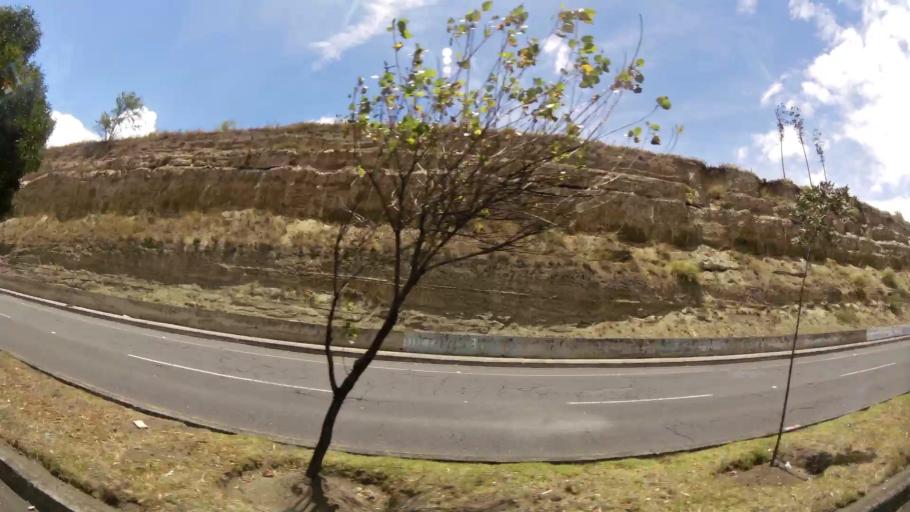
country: EC
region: Tungurahua
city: Pelileo
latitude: -1.3099
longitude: -78.5992
